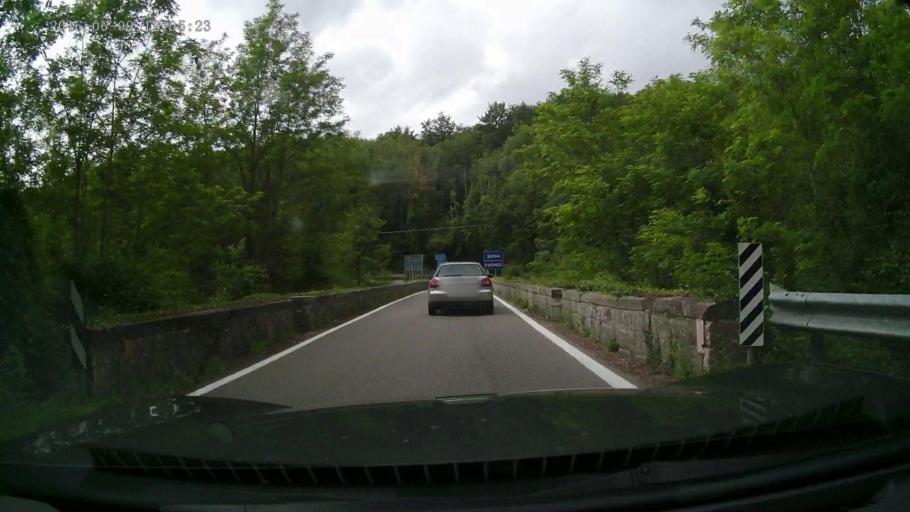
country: IT
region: Tuscany
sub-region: Province of Florence
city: Panzano in Chianti
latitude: 43.5202
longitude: 11.2926
